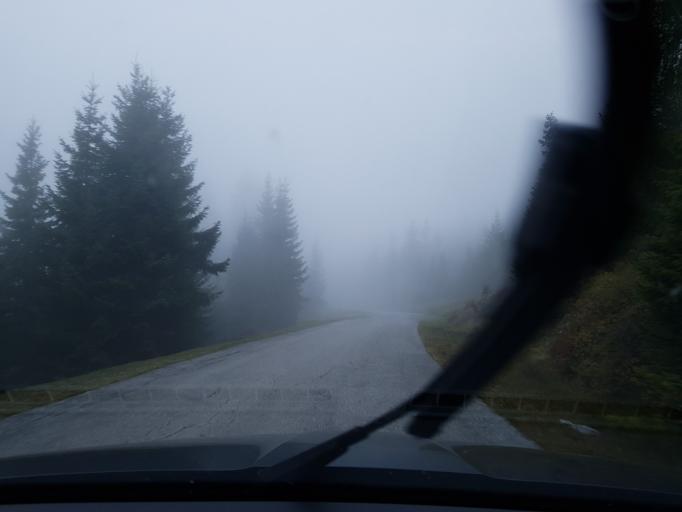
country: AT
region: Salzburg
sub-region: Politischer Bezirk Sankt Johann im Pongau
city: Radstadt
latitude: 47.4102
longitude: 13.4817
